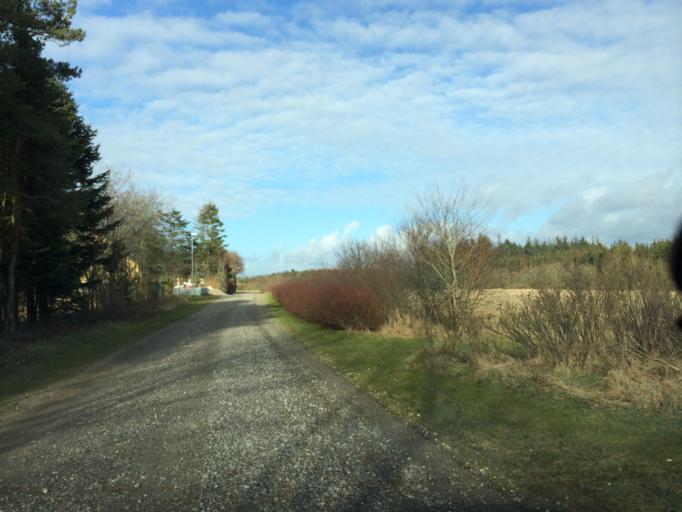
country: DK
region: Central Jutland
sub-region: Holstebro Kommune
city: Ulfborg
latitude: 56.2681
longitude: 8.3253
